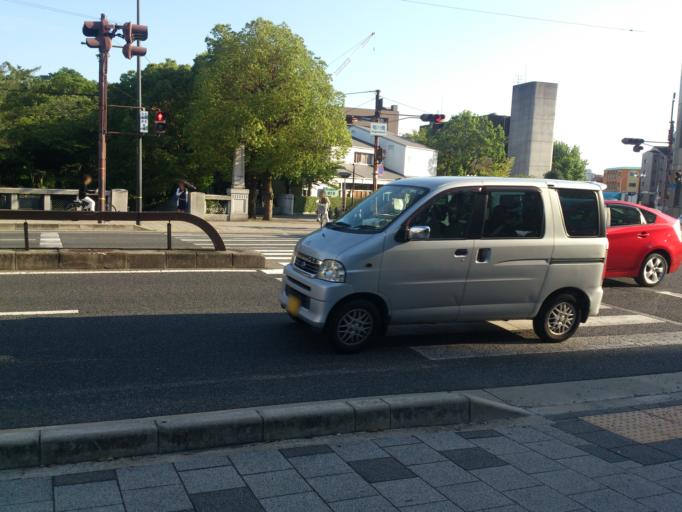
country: JP
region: Hyogo
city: Amagasaki
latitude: 34.7197
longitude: 135.4287
